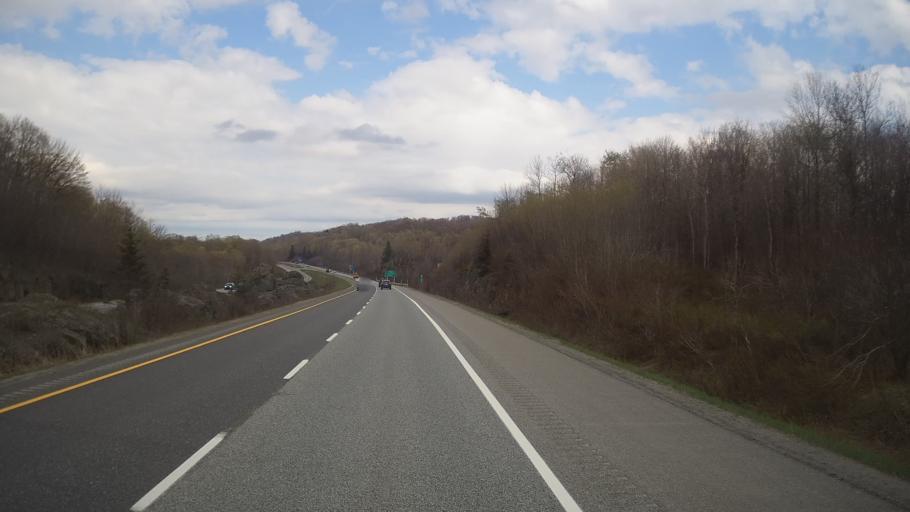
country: CA
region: Quebec
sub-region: Estrie
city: Magog
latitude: 45.2894
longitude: -72.2593
